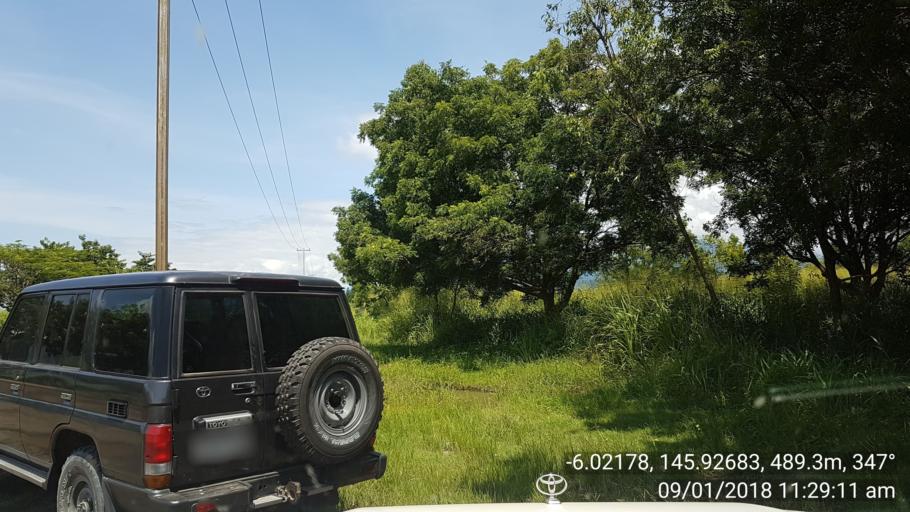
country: PG
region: Eastern Highlands
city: Kainantu
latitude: -6.0218
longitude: 145.9270
